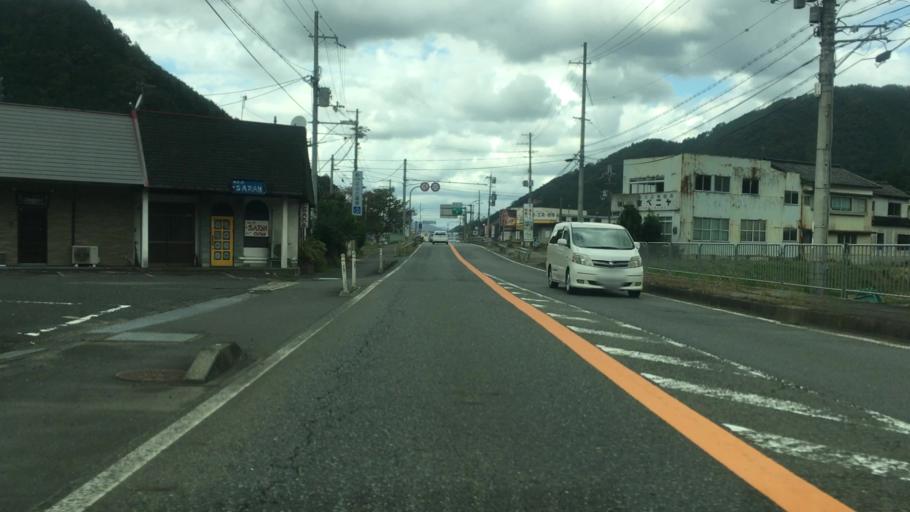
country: JP
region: Hyogo
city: Toyooka
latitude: 35.3196
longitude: 134.8814
